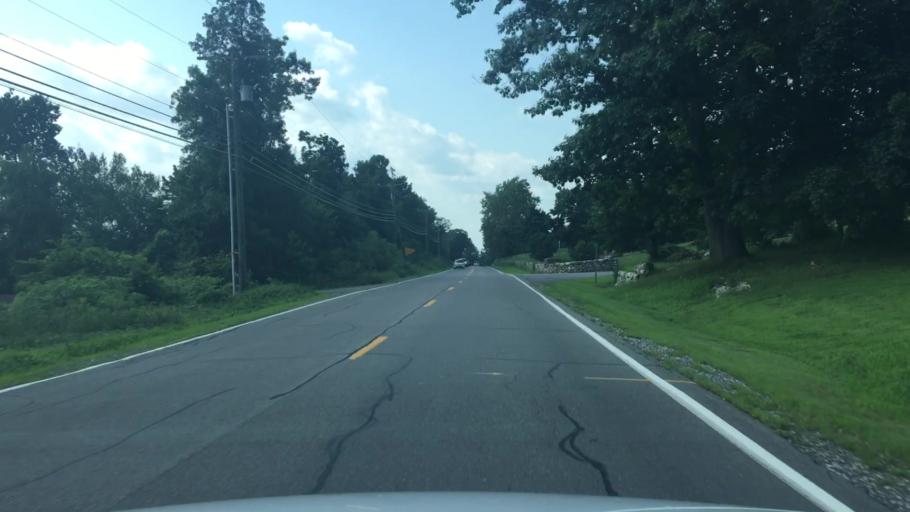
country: US
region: New Hampshire
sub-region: Rockingham County
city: Auburn
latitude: 42.9708
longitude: -71.3655
